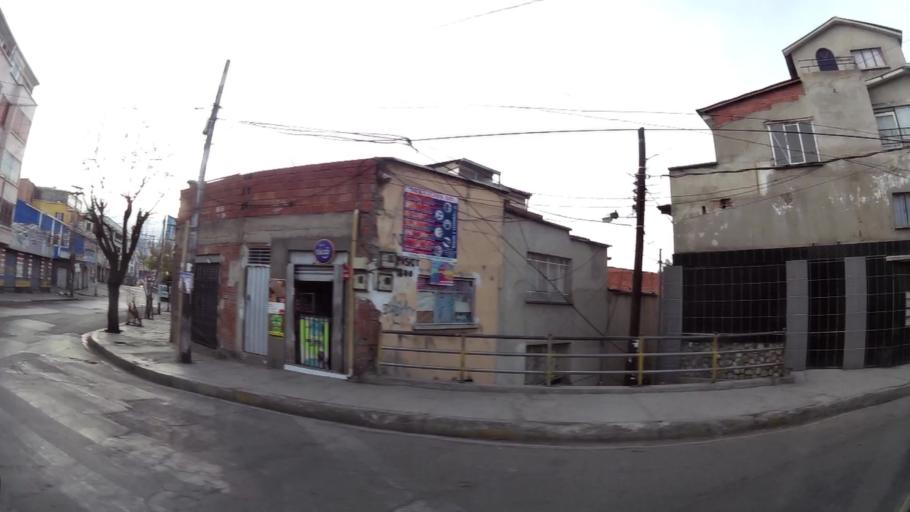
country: BO
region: La Paz
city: La Paz
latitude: -16.4993
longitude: -68.1278
